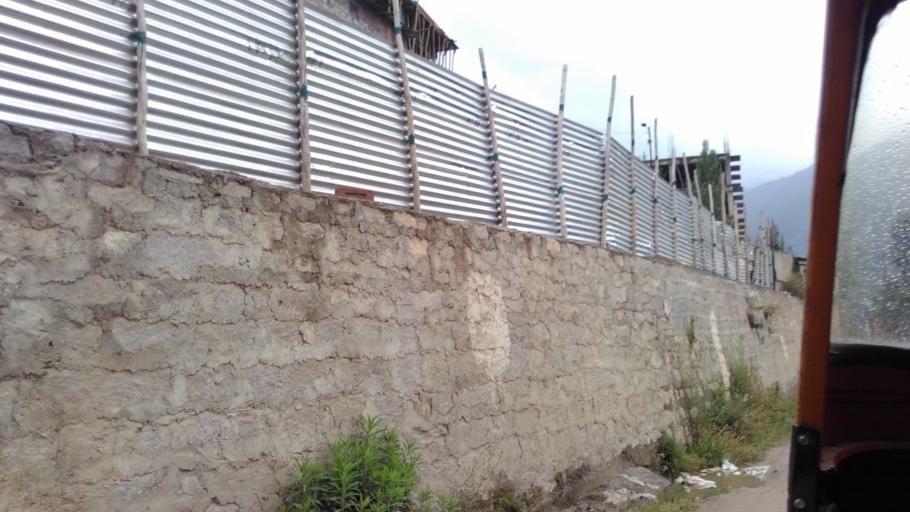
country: IN
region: Himachal Pradesh
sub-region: Kulu
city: Manali
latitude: 32.2253
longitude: 77.1850
